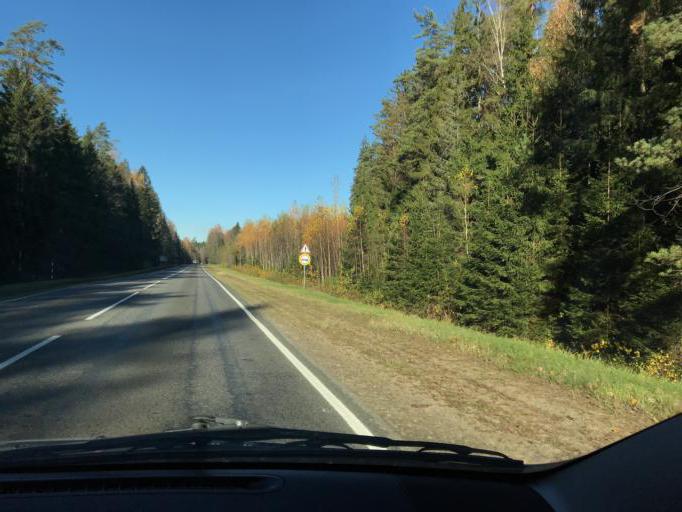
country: BY
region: Vitebsk
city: Polatsk
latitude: 55.4146
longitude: 28.7963
